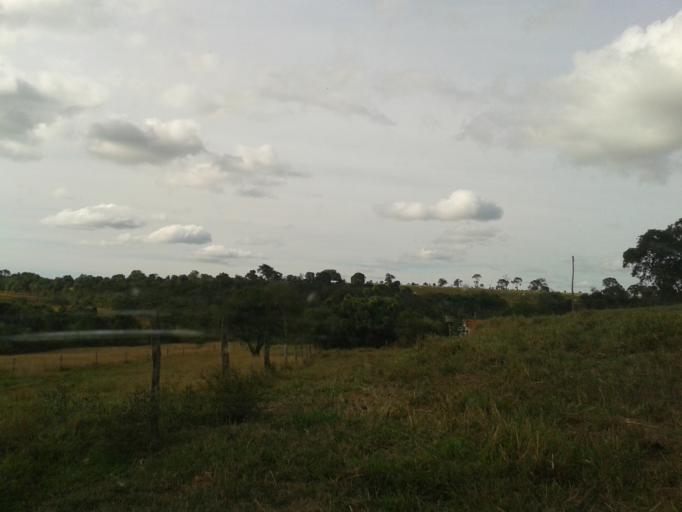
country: BR
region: Minas Gerais
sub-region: Campina Verde
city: Campina Verde
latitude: -19.4411
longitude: -49.7342
